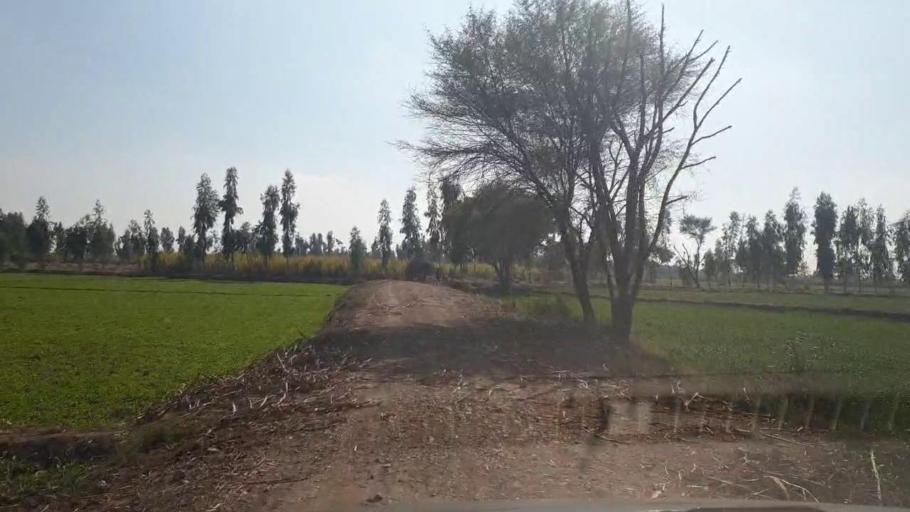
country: PK
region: Sindh
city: Shahdadpur
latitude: 25.9252
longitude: 68.5752
